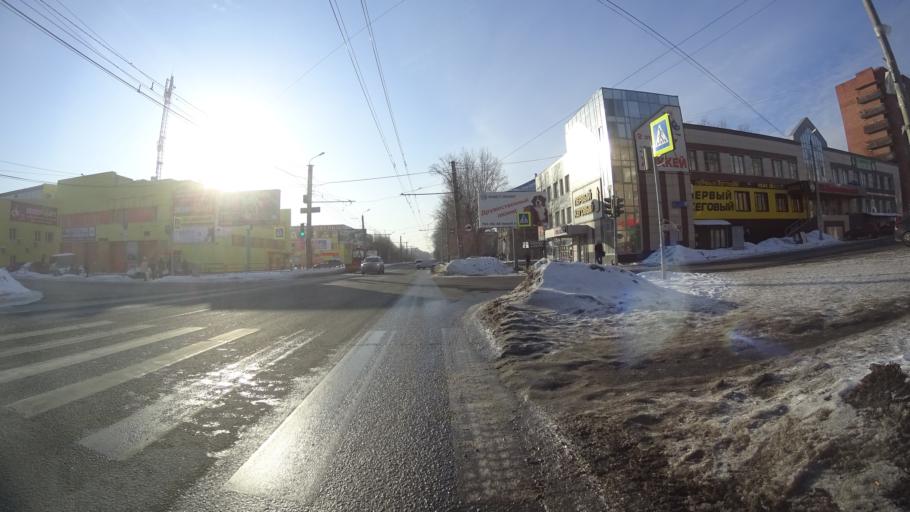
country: RU
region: Chelyabinsk
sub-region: Gorod Chelyabinsk
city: Chelyabinsk
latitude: 55.1830
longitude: 61.4547
